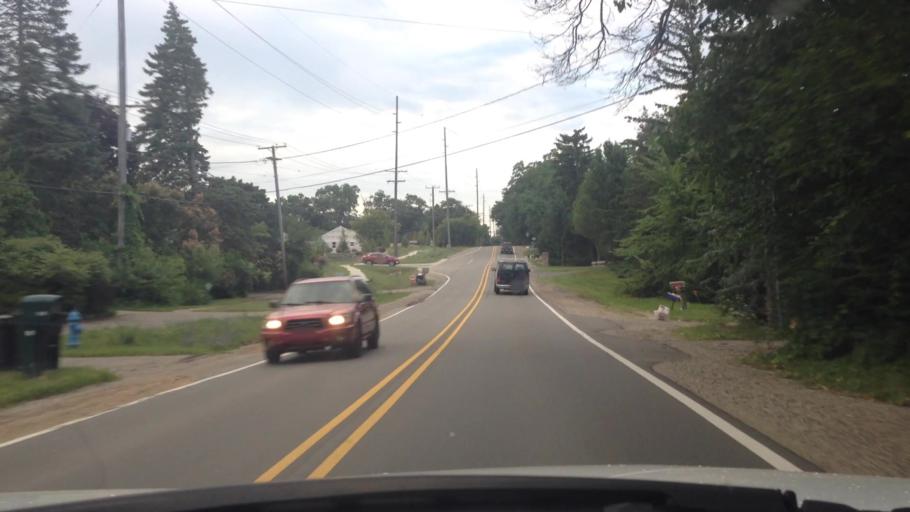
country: US
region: Michigan
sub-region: Oakland County
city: Waterford
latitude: 42.6966
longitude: -83.3485
